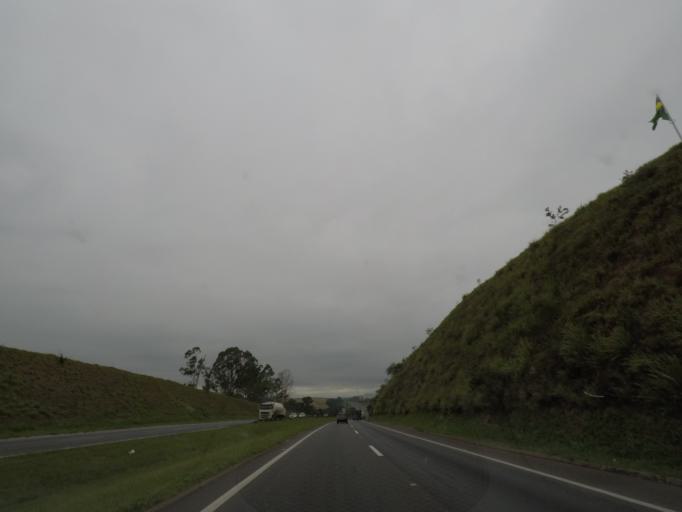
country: BR
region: Sao Paulo
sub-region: Jarinu
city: Jarinu
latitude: -23.0360
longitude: -46.7137
